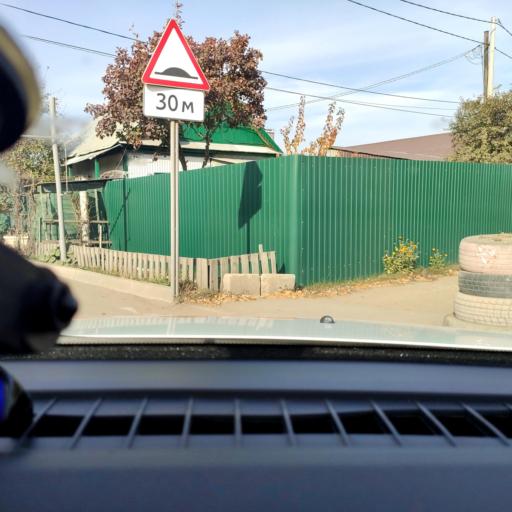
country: RU
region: Samara
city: Smyshlyayevka
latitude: 53.2281
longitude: 50.3035
